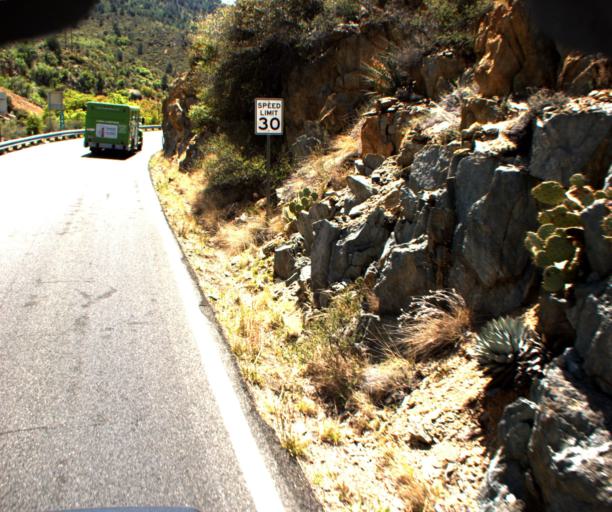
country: US
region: Arizona
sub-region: Yavapai County
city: Clarkdale
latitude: 34.7413
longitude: -112.1217
